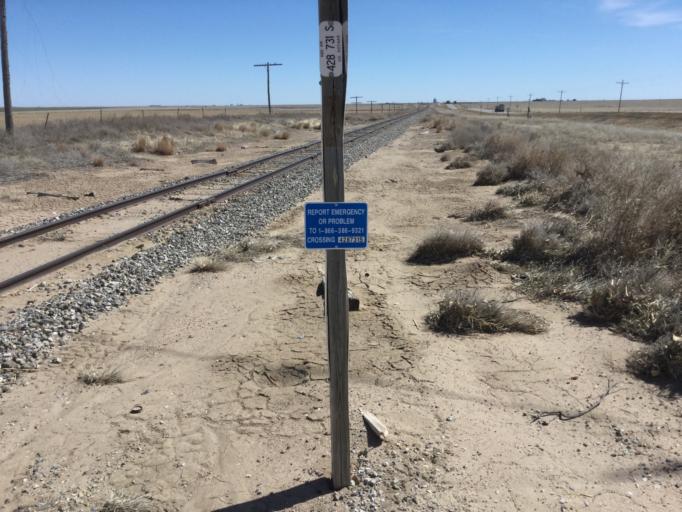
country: US
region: Kansas
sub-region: Greeley County
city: Tribune
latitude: 38.4609
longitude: -101.7152
